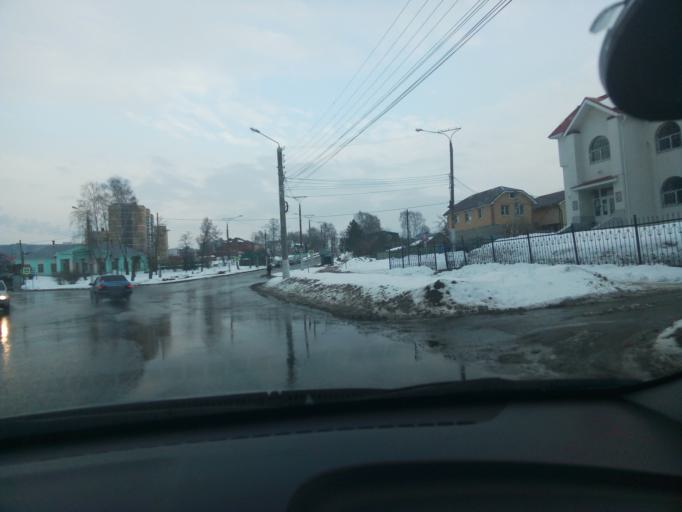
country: RU
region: Chuvashia
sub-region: Cheboksarskiy Rayon
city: Cheboksary
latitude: 56.1342
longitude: 47.2295
